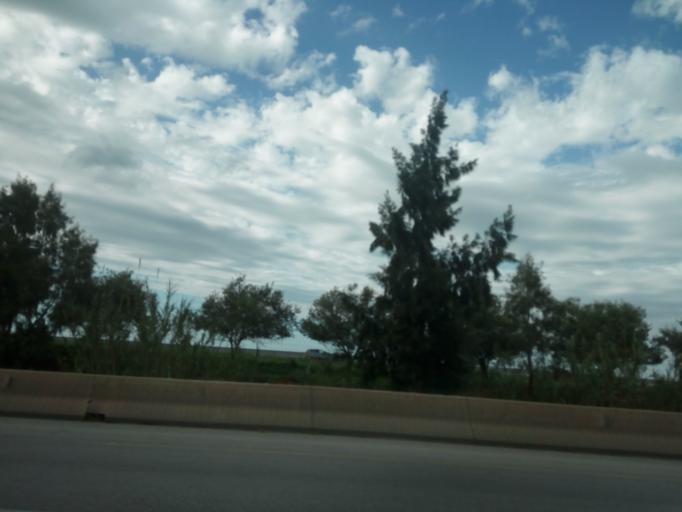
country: DZ
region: Tipaza
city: Mouzaia
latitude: 36.4498
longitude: 2.6656
